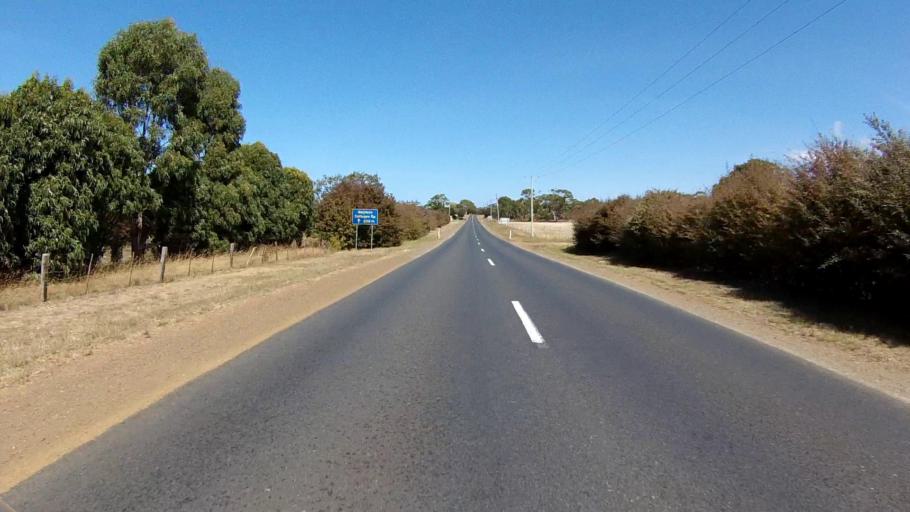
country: AU
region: Tasmania
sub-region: Sorell
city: Sorell
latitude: -42.1353
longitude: 148.0712
